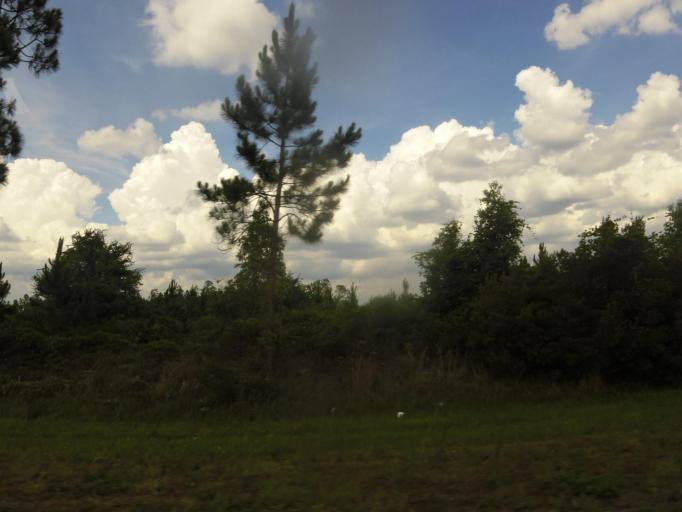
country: US
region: Florida
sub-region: Baker County
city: Macclenny
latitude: 30.2063
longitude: -82.0576
